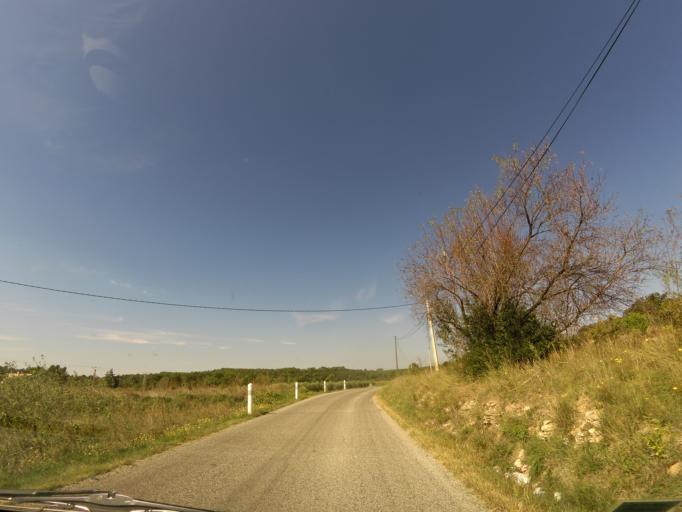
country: FR
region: Languedoc-Roussillon
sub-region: Departement du Gard
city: Uchaud
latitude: 43.7605
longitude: 4.2585
